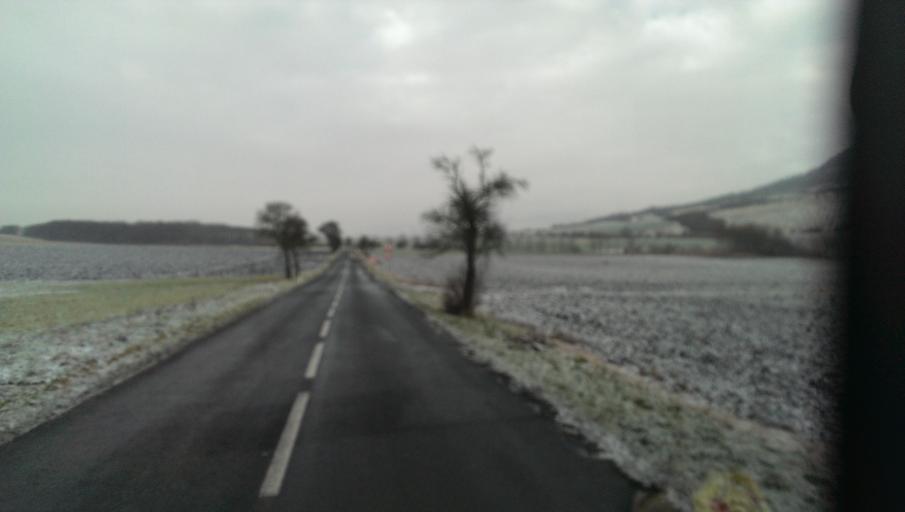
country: CZ
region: Ustecky
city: Libochovice
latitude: 50.4187
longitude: 14.0224
